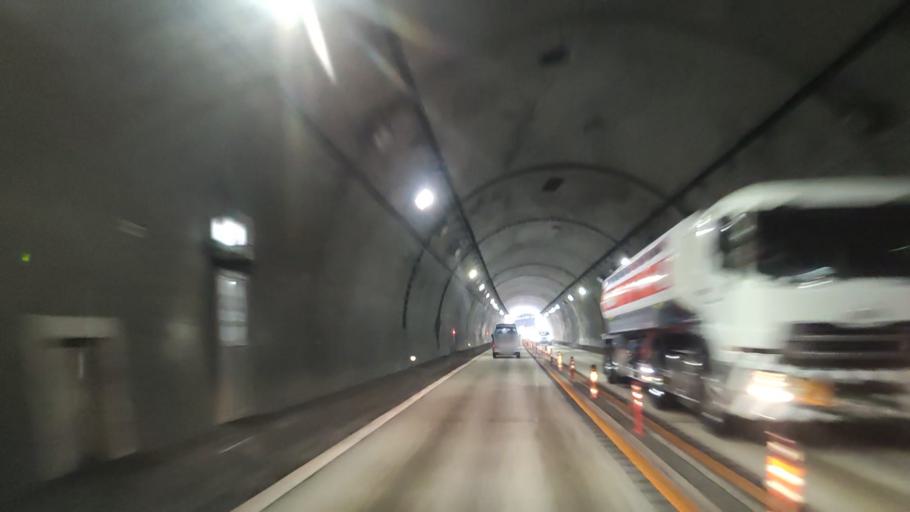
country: JP
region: Tokushima
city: Kamojimacho-jogejima
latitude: 34.1111
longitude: 134.3196
